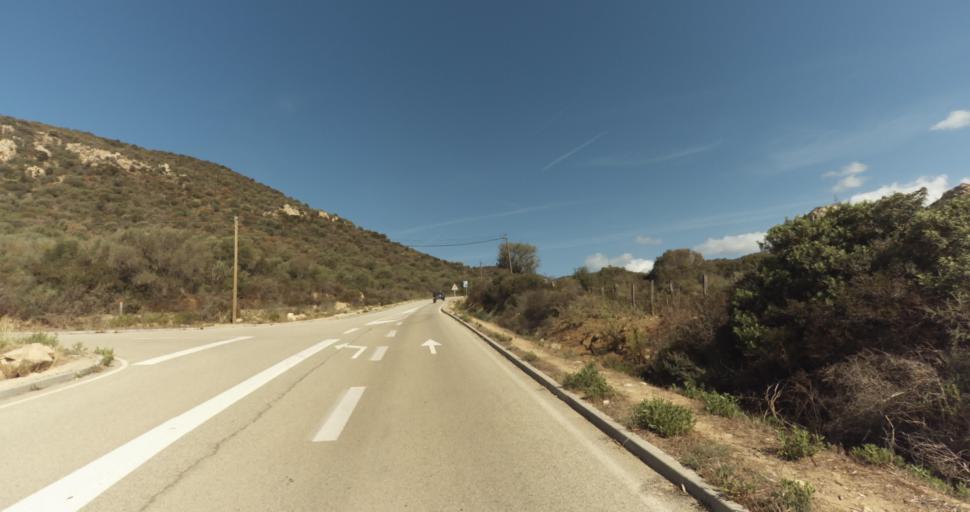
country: FR
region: Corsica
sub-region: Departement de la Corse-du-Sud
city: Ajaccio
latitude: 41.9118
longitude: 8.6440
